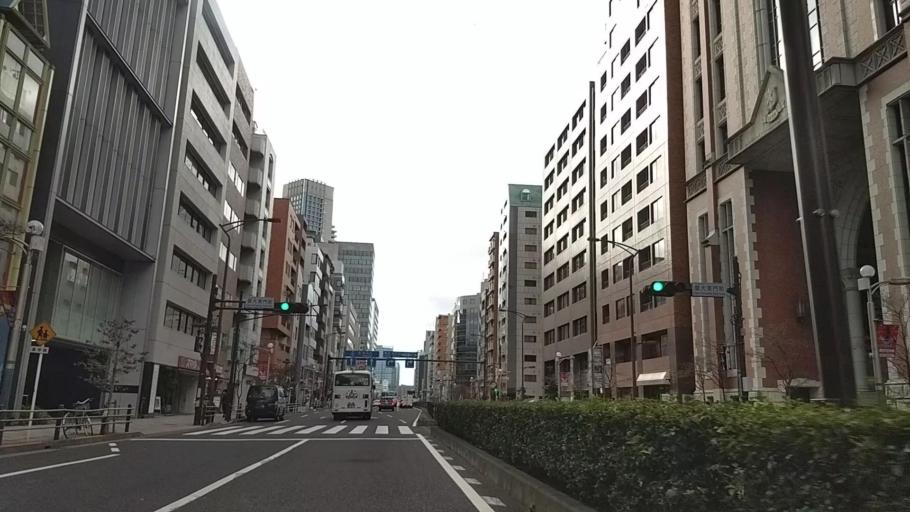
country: JP
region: Tokyo
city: Tokyo
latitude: 35.6495
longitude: 139.7448
